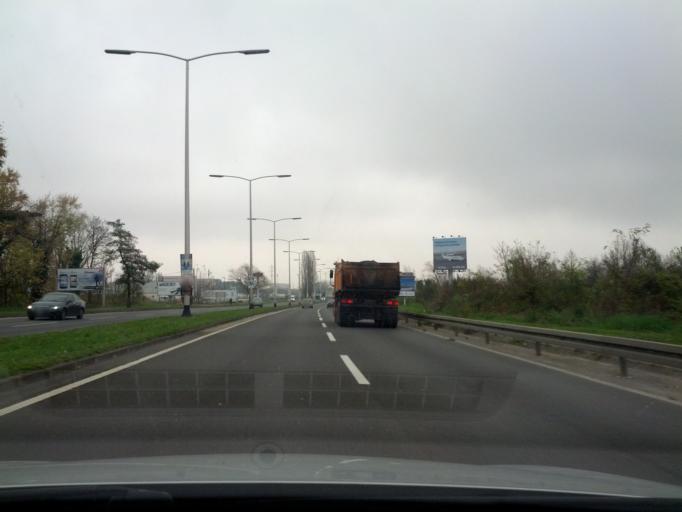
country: HR
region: Grad Zagreb
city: Stenjevec
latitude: 45.7970
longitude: 15.8687
